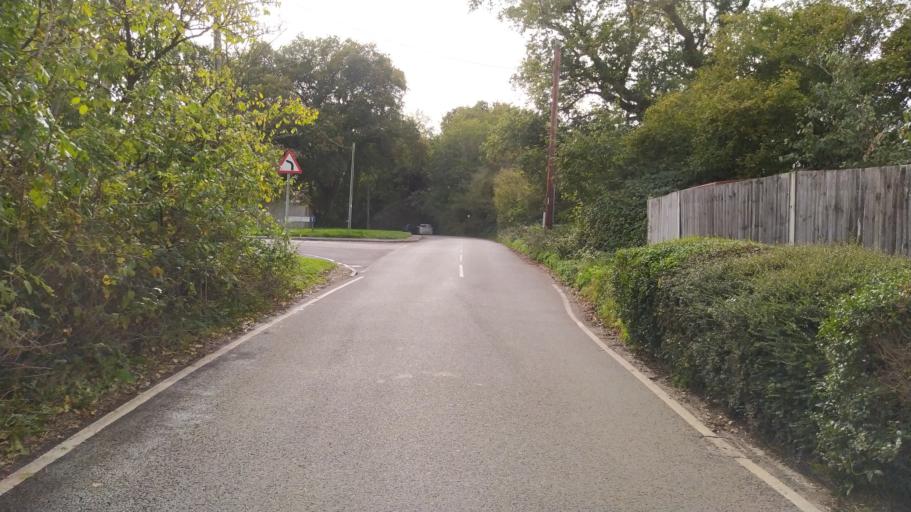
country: GB
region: England
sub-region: Hampshire
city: Romsey
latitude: 51.0175
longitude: -1.5445
